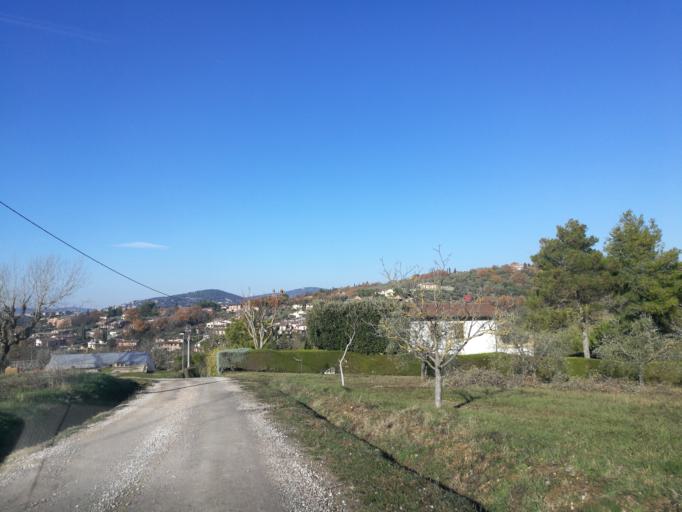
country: IT
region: Umbria
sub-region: Provincia di Perugia
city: Perugia
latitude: 43.0770
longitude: 12.3877
